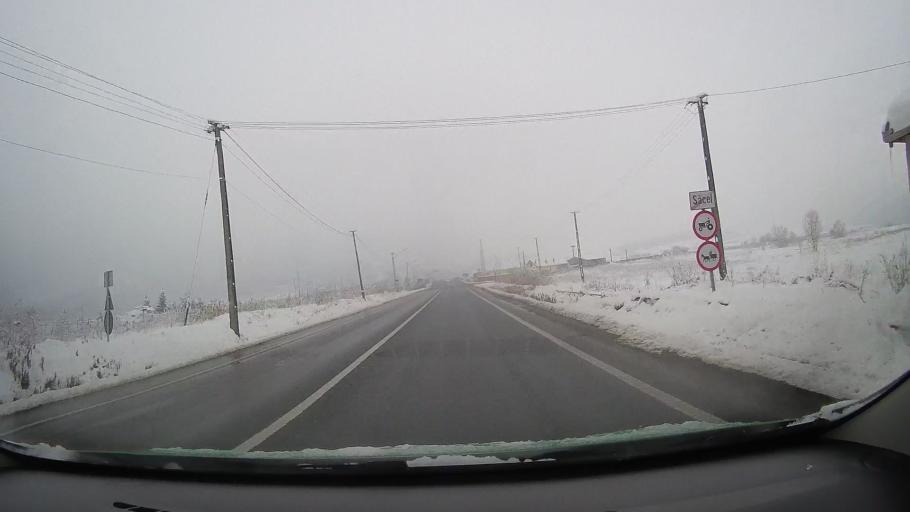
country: RO
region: Sibiu
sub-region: Comuna Orlat
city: Orlat
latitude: 45.7828
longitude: 23.9426
